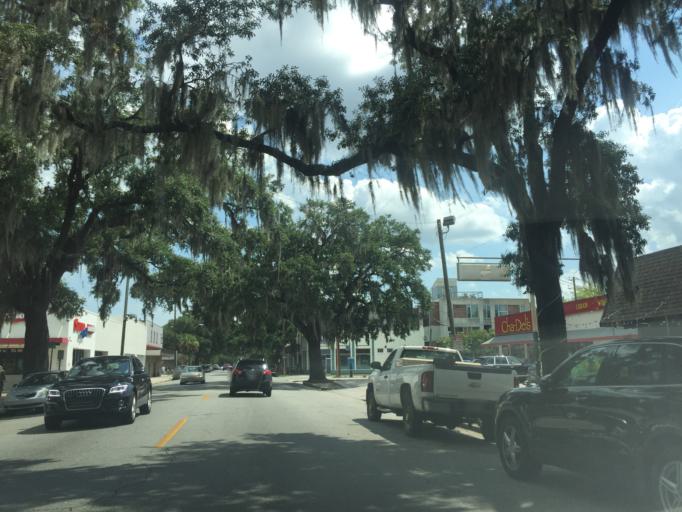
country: US
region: Georgia
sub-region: Chatham County
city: Savannah
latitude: 32.0555
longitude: -81.1009
